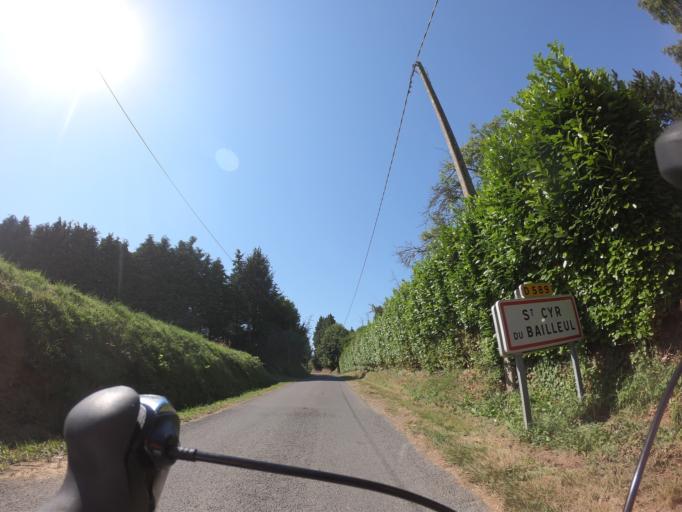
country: FR
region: Lower Normandy
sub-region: Departement de la Manche
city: Barenton
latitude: 48.5674
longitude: -0.7996
